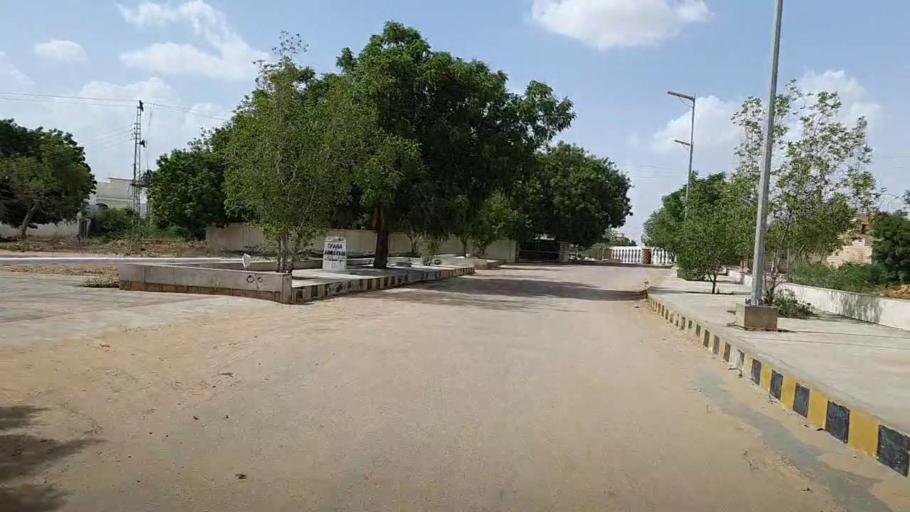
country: PK
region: Sindh
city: Jamshoro
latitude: 25.4070
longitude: 67.7844
